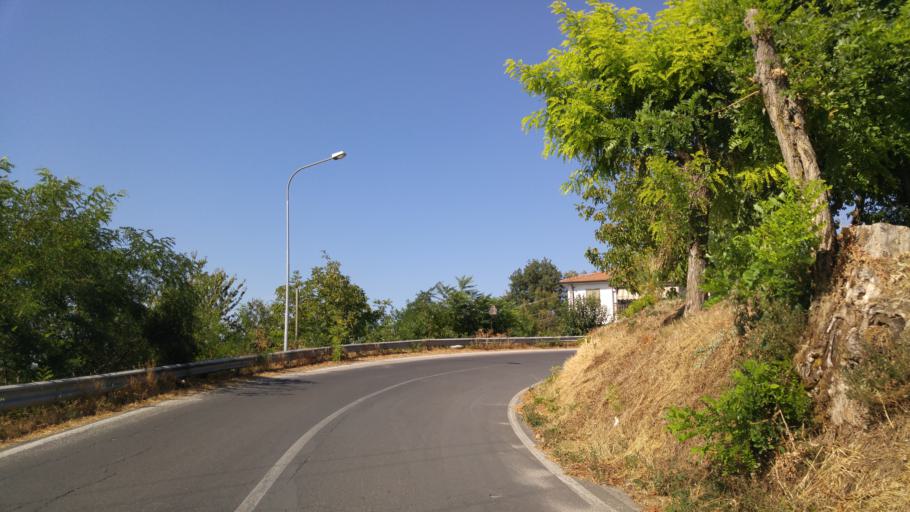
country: IT
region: The Marches
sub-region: Provincia di Pesaro e Urbino
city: Barchi
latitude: 43.6735
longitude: 12.9269
